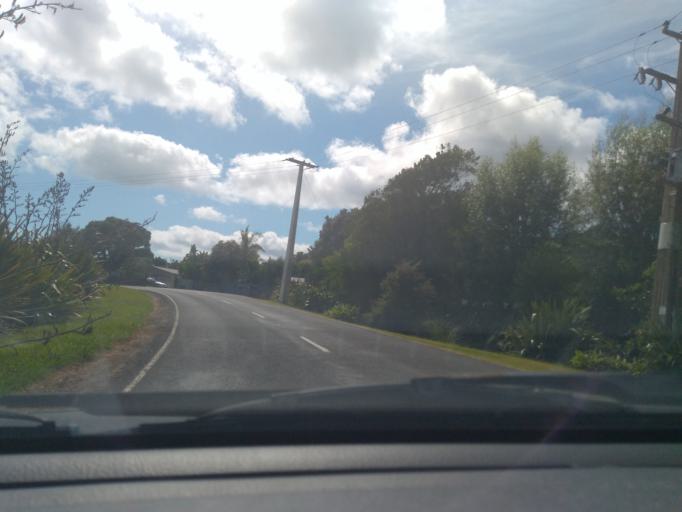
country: NZ
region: Northland
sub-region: Far North District
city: Taipa
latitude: -34.9931
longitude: 173.7073
